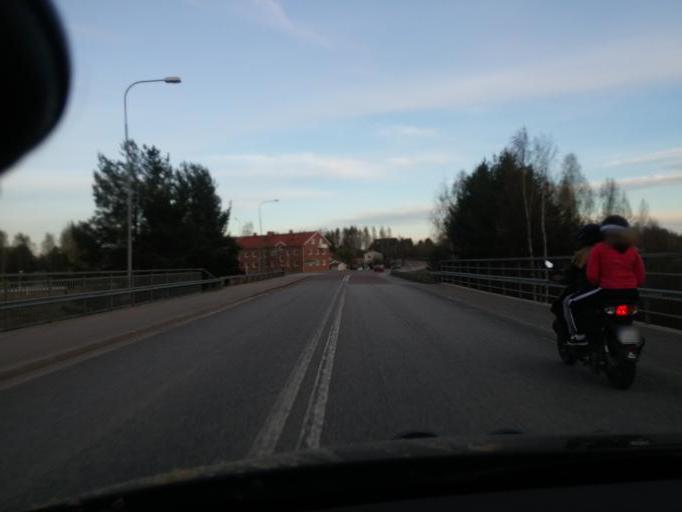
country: SE
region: Gaevleborg
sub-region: Ljusdals Kommun
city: Ljusdal
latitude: 61.8341
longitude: 16.0677
